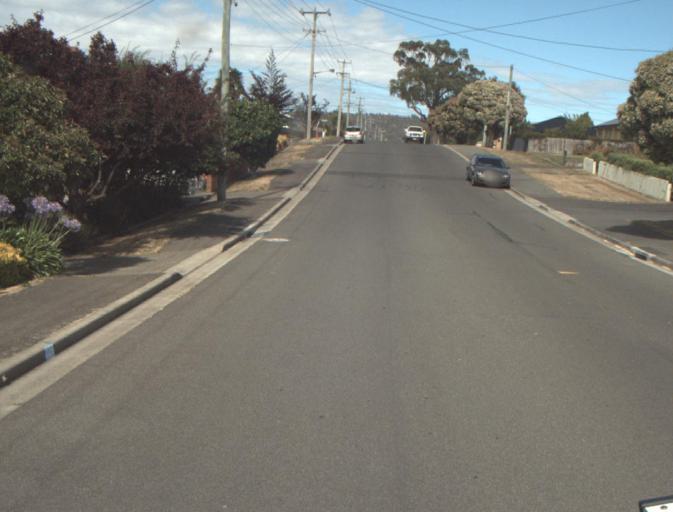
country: AU
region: Tasmania
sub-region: Launceston
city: Summerhill
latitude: -41.4691
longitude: 147.1248
